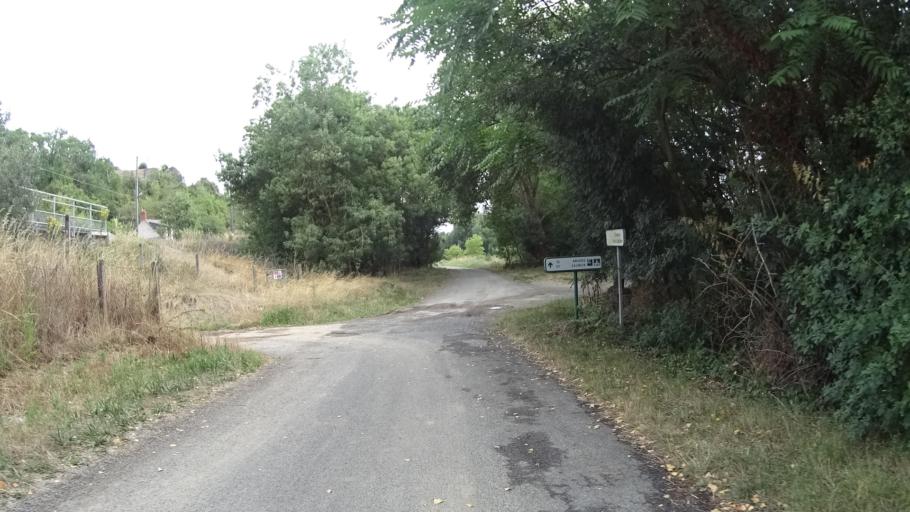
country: FR
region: Pays de la Loire
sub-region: Departement de Maine-et-Loire
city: Savennieres
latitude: 47.3871
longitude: -0.6415
